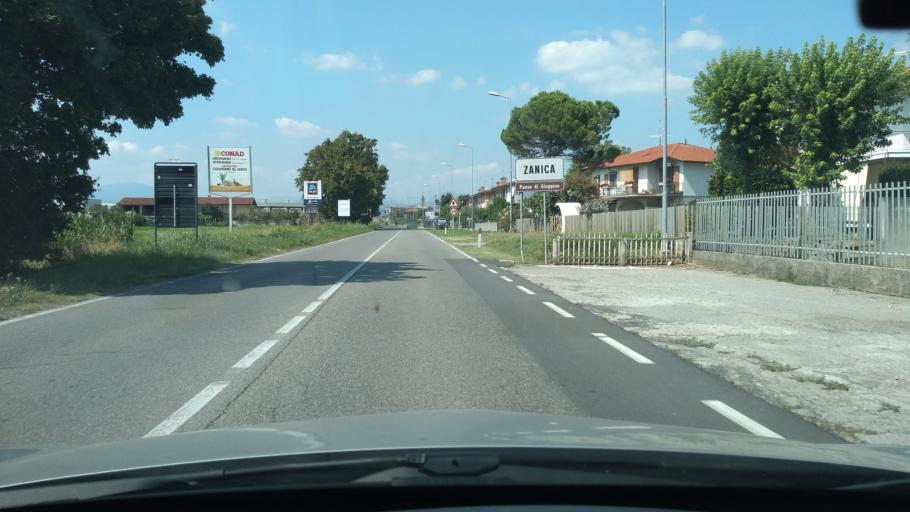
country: IT
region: Lombardy
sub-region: Provincia di Bergamo
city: Zanica
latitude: 45.6310
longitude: 9.6871
